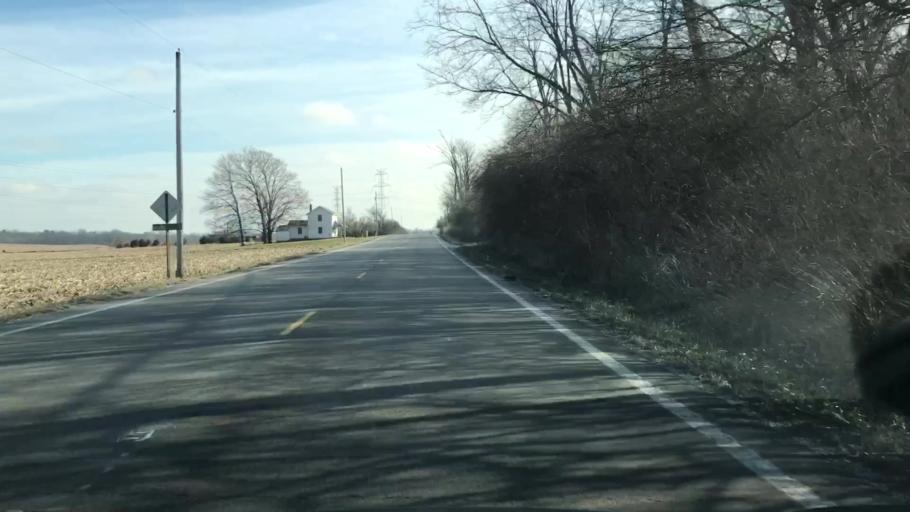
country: US
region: Ohio
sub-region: Greene County
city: Fairborn
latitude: 39.8079
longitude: -83.9774
